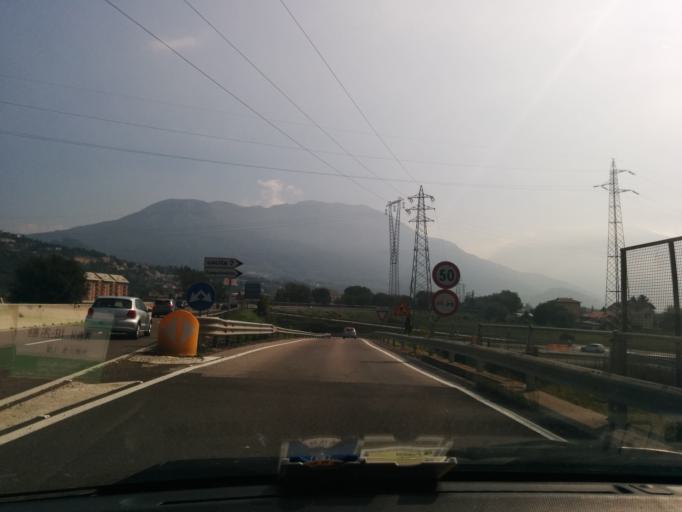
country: IT
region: Trentino-Alto Adige
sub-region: Provincia di Trento
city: Trento
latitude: 46.0842
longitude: 11.1105
